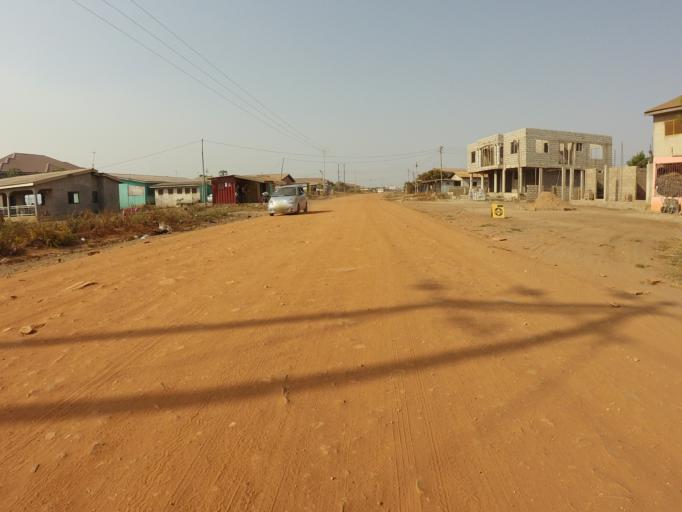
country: GH
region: Greater Accra
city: Tema
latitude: 5.7015
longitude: 0.0577
